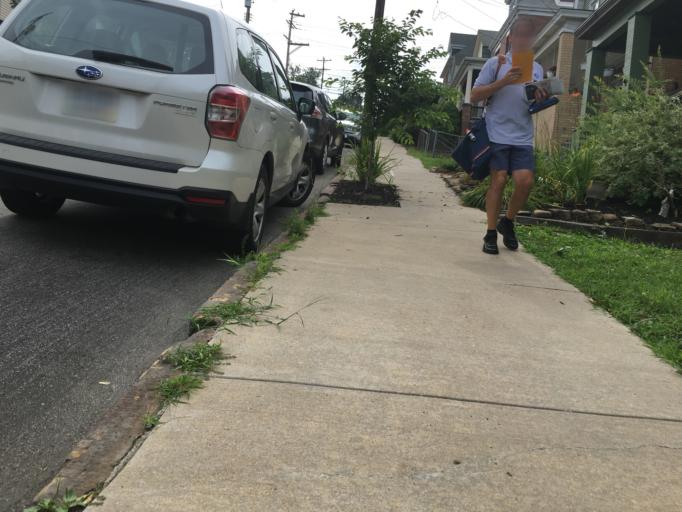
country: US
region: Pennsylvania
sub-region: Allegheny County
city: Swissvale
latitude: 40.4239
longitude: -79.8839
